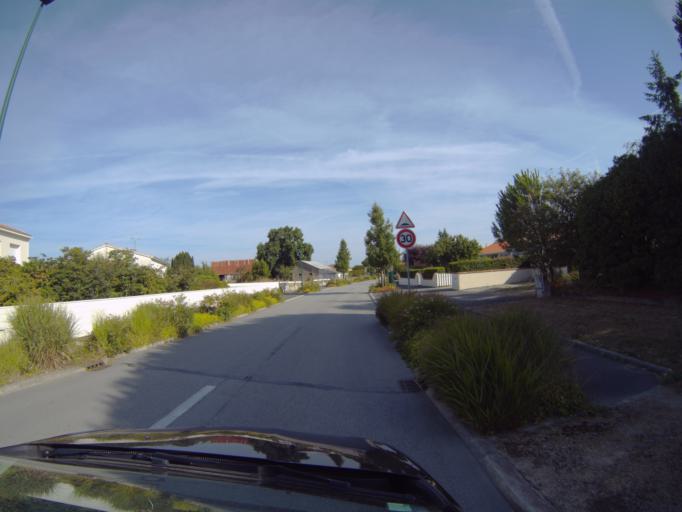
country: FR
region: Pays de la Loire
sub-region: Departement de la Vendee
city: Les Clouzeaux
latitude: 46.6251
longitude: -1.5074
